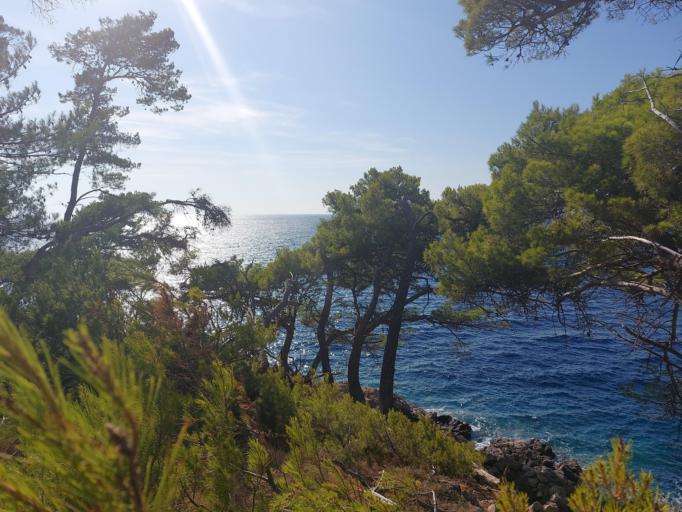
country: HR
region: Dubrovacko-Neretvanska
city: Smokvica
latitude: 42.7241
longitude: 16.8416
